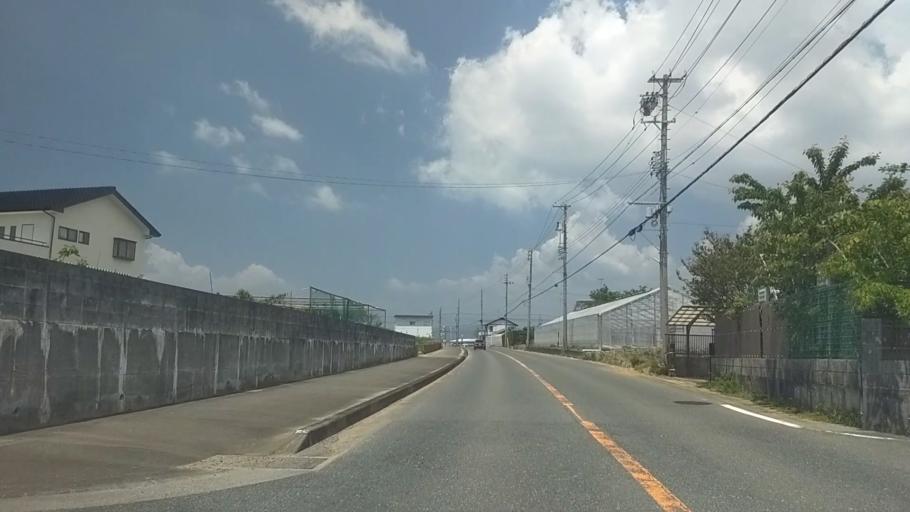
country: JP
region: Shizuoka
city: Hamamatsu
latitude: 34.7553
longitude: 137.6804
